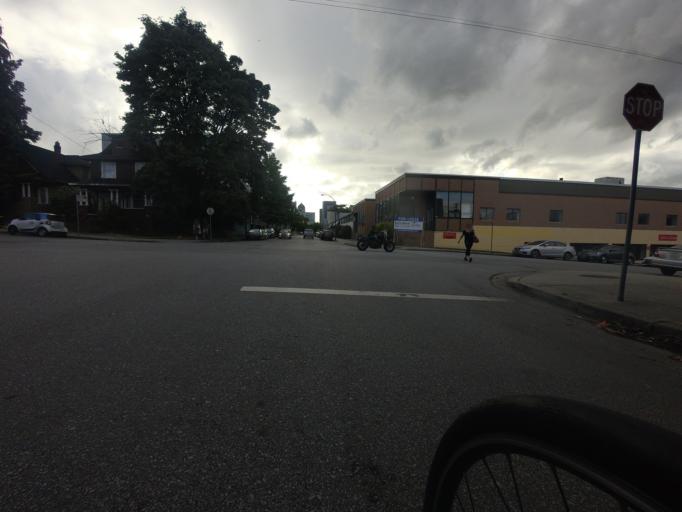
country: CA
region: British Columbia
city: Vancouver
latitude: 49.2639
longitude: -123.1107
